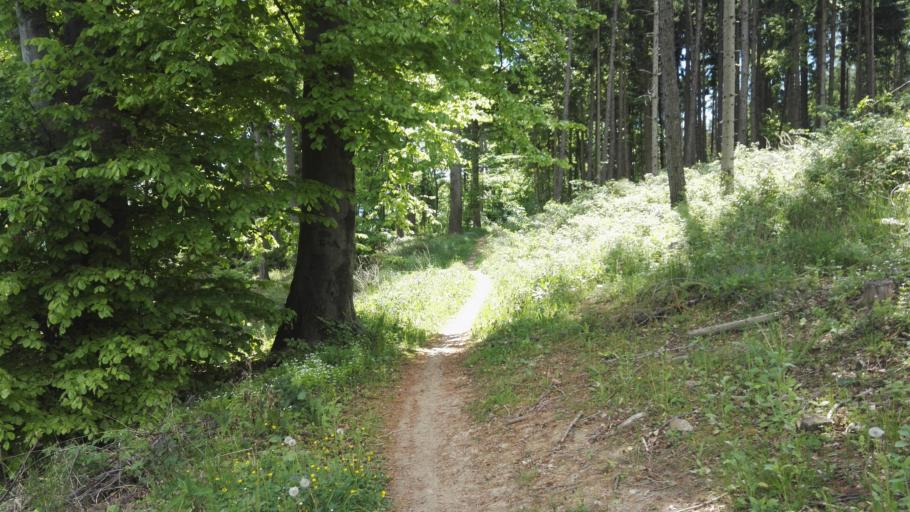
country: AT
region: Styria
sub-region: Graz Stadt
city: Goesting
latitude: 47.0901
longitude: 15.3873
